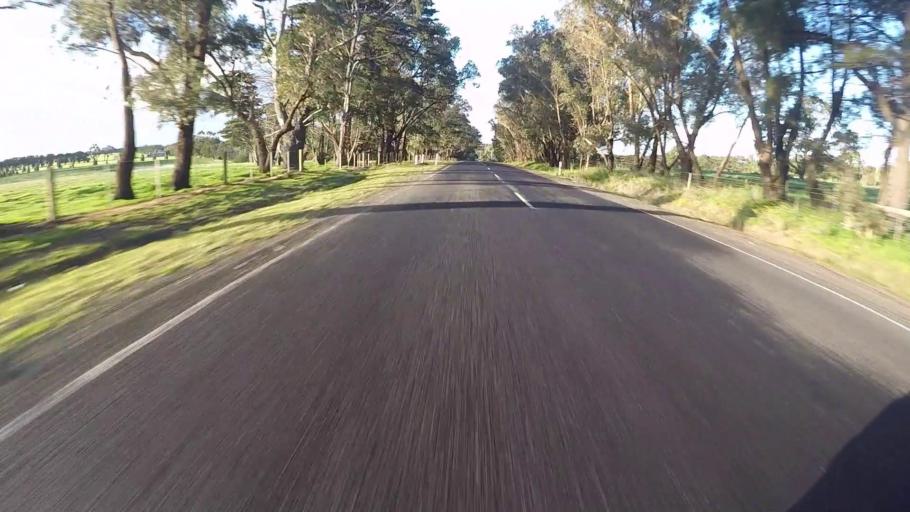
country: AU
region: Victoria
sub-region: Greater Geelong
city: Wandana Heights
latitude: -38.1493
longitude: 144.1786
